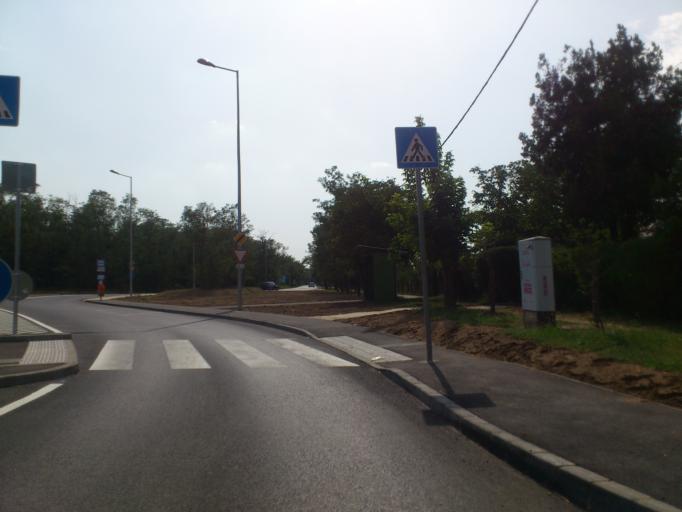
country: HU
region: Budapest
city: Budapest XVII. keruelet
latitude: 47.4533
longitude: 19.2293
